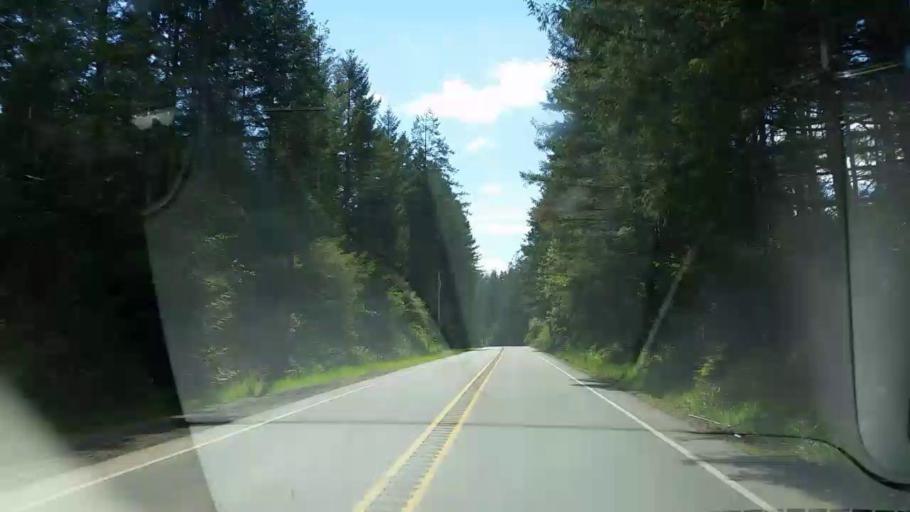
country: US
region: Washington
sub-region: Mason County
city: Allyn
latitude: 47.3700
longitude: -122.7836
